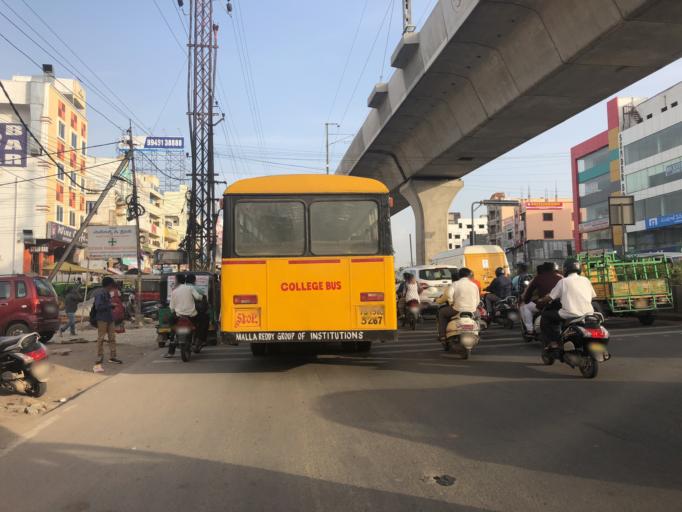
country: IN
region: Telangana
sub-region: Rangareddi
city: Kukatpalli
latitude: 17.4700
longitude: 78.4275
